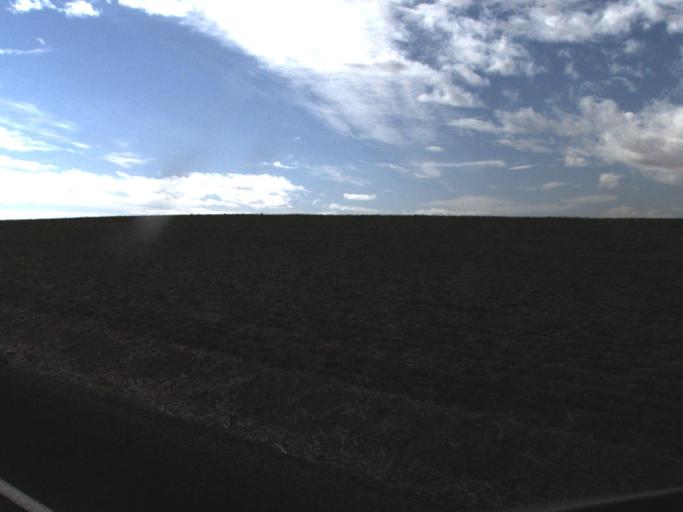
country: US
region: Washington
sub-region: Okanogan County
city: Coulee Dam
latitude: 47.8105
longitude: -118.7218
